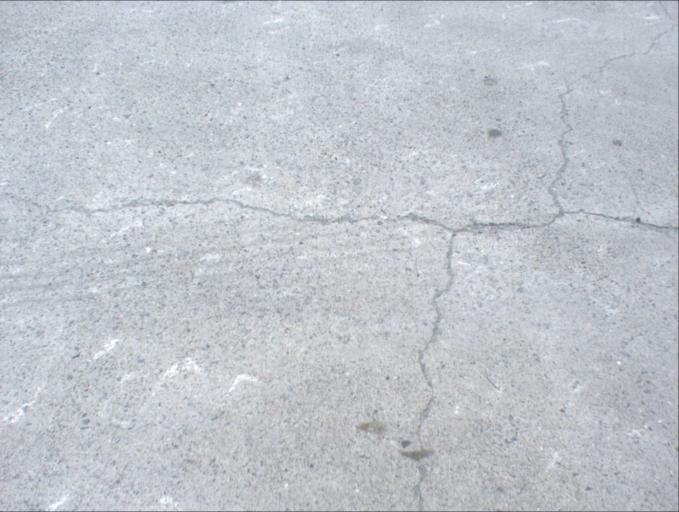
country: AU
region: Queensland
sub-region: Logan
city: Beenleigh
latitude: -27.7100
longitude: 153.1856
